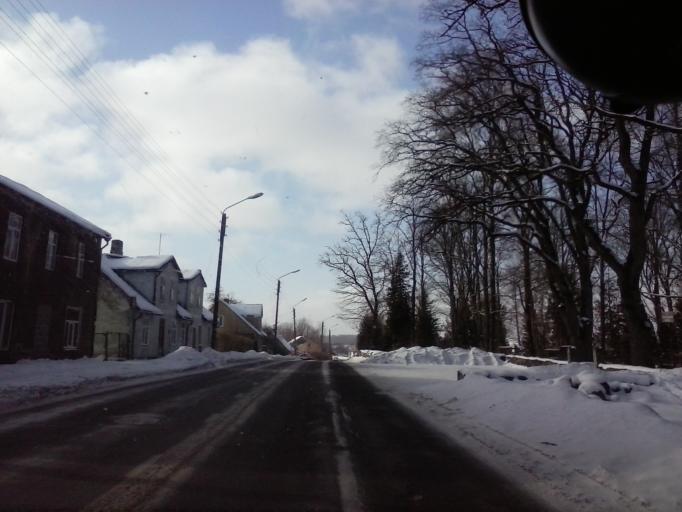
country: EE
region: Viljandimaa
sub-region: Viljandi linn
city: Viljandi
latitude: 58.3586
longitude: 25.5702
